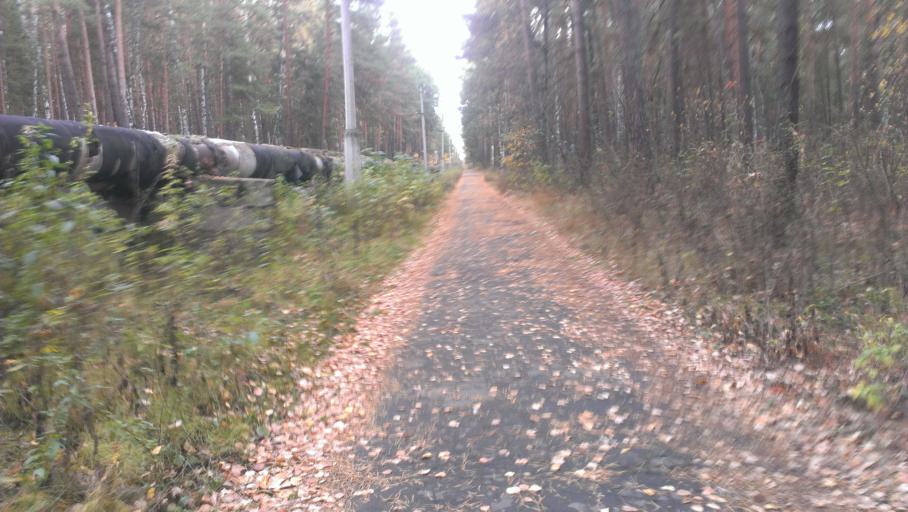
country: RU
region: Altai Krai
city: Yuzhnyy
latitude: 53.2680
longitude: 83.6827
